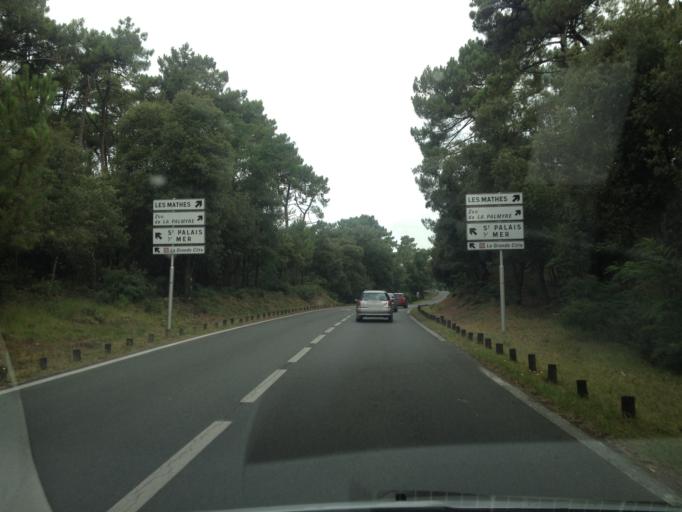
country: FR
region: Poitou-Charentes
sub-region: Departement de la Charente-Maritime
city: Saint-Palais-sur-Mer
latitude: 45.6577
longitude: -1.1224
